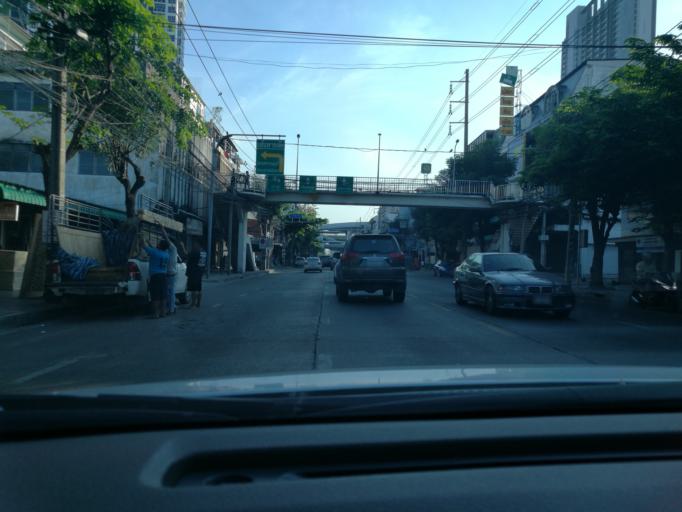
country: TH
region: Bangkok
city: Bang Sue
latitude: 13.8099
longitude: 100.5218
